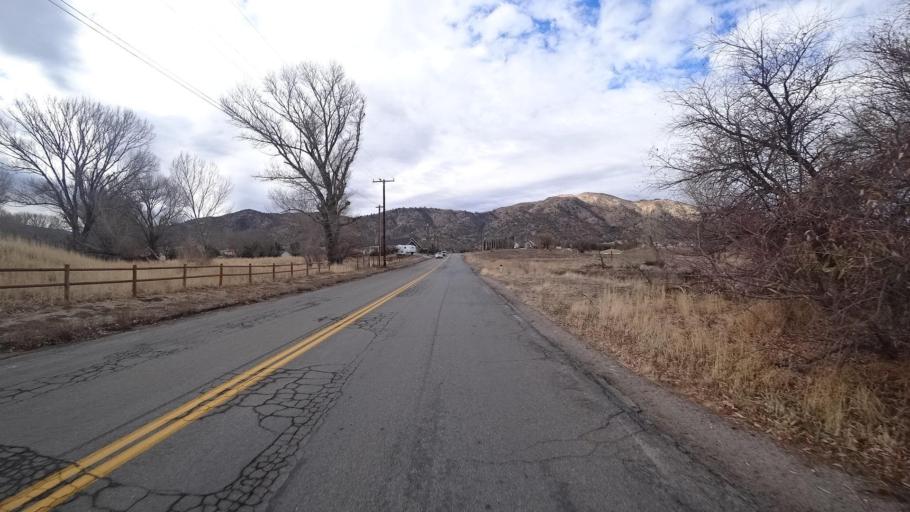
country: US
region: California
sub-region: Kern County
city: Golden Hills
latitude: 35.1540
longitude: -118.4971
